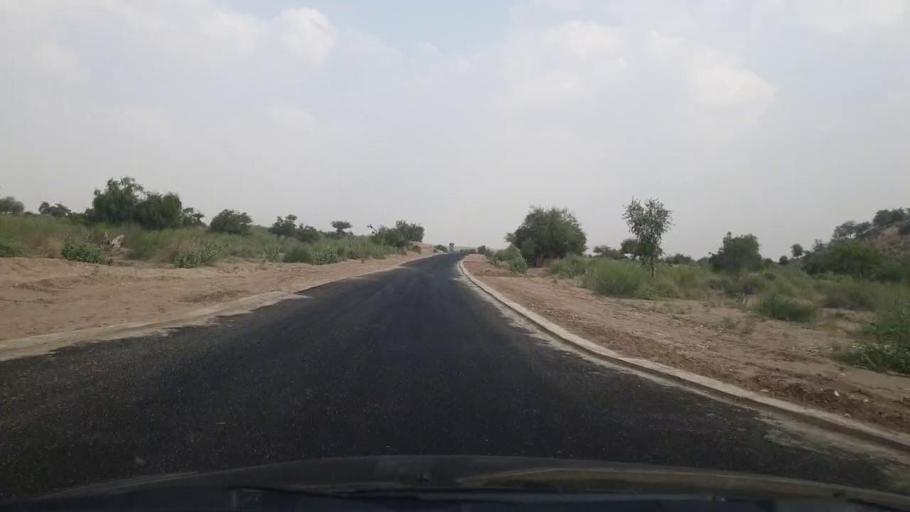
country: PK
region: Sindh
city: Islamkot
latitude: 25.0039
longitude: 70.6637
